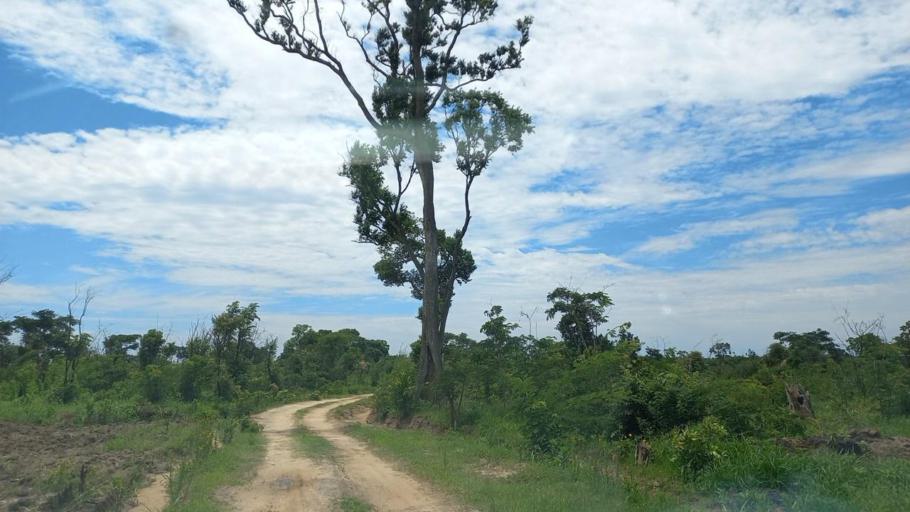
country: ZM
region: Copperbelt
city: Kitwe
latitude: -12.8089
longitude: 28.4010
